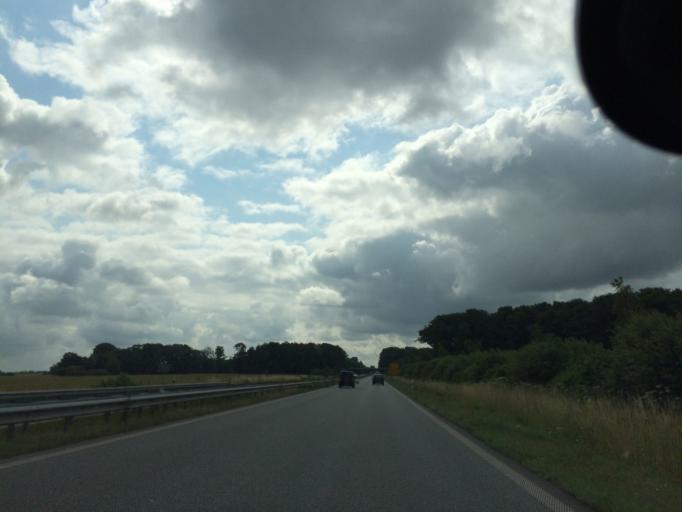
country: DE
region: Schleswig-Holstein
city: Tuttendorf
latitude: 54.3965
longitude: 10.0112
